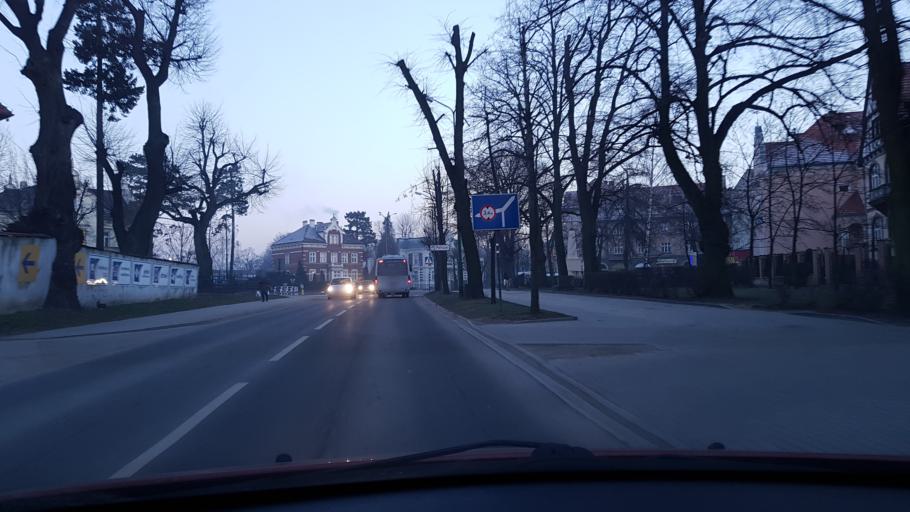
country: PL
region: Lower Silesian Voivodeship
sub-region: Powiat zabkowicki
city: Zabkowice Slaskie
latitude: 50.5952
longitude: 16.8114
